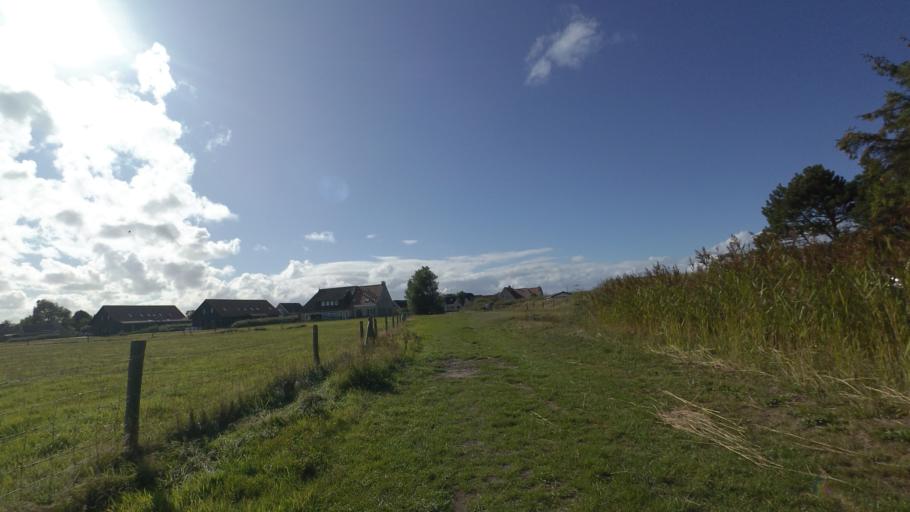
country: NL
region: Friesland
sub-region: Gemeente Ameland
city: Nes
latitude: 53.4511
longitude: 5.8034
